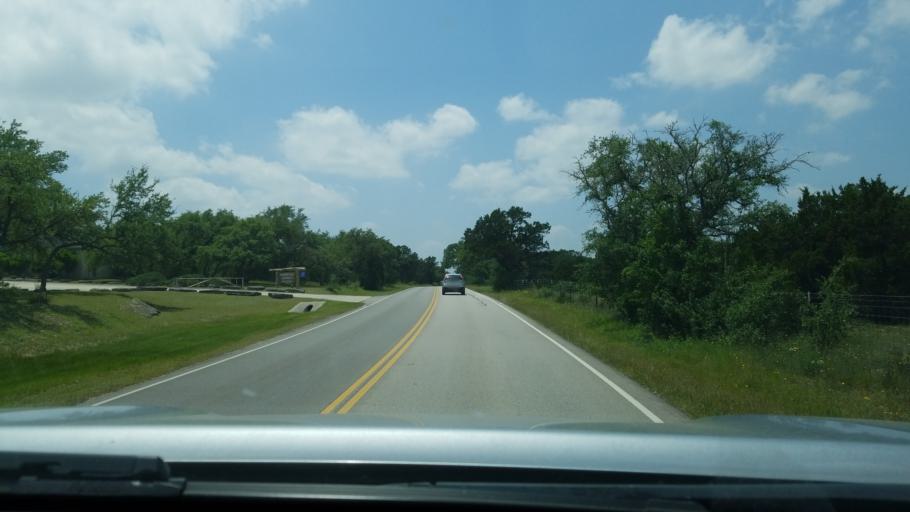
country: US
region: Texas
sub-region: Hays County
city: Woodcreek
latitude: 30.0420
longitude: -98.1100
